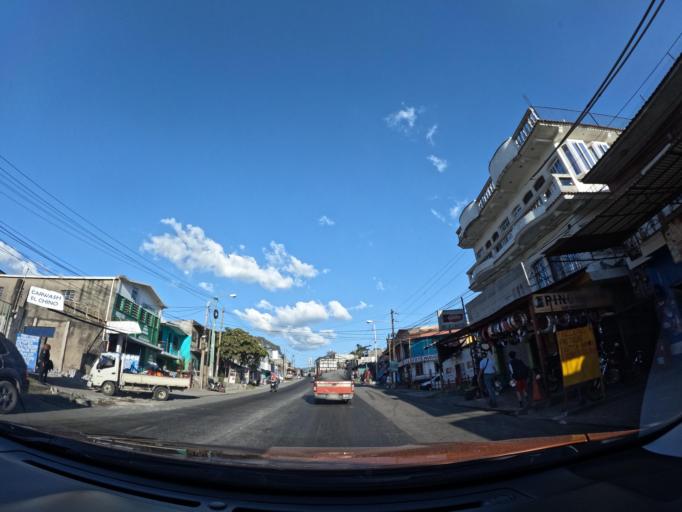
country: GT
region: Escuintla
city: Palin
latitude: 14.4040
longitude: -90.6947
